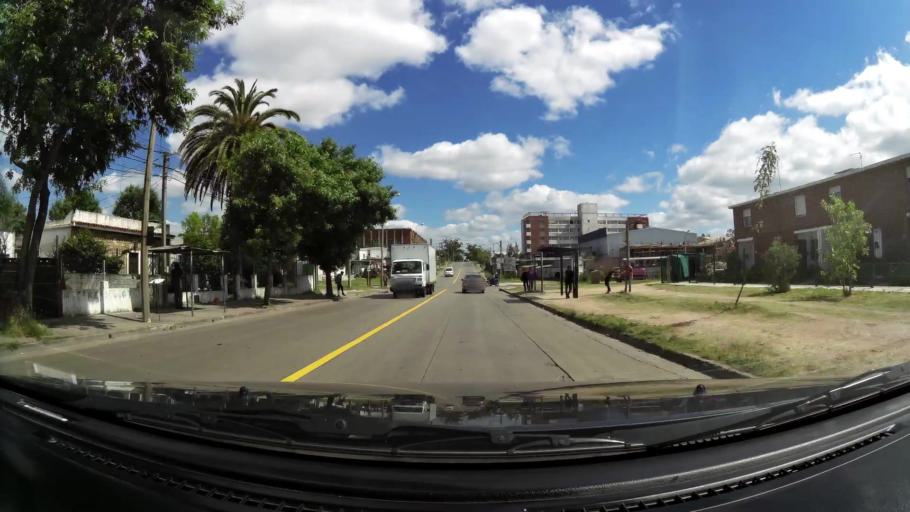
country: UY
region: Canelones
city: Paso de Carrasco
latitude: -34.8617
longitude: -56.1236
